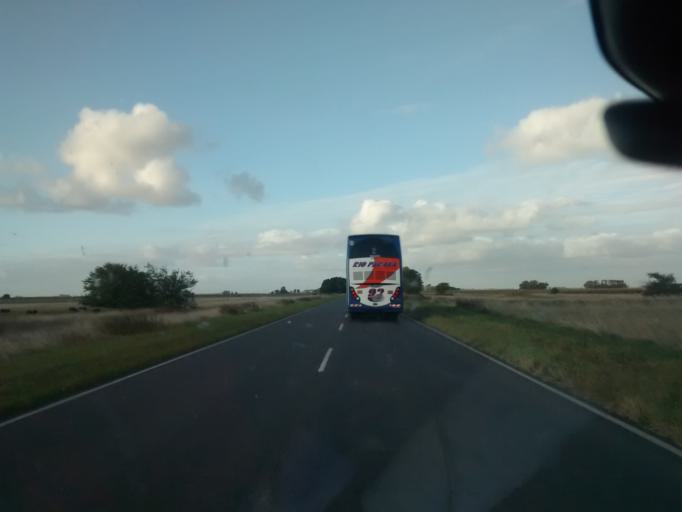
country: AR
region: Buenos Aires
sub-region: Partido de General Belgrano
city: General Belgrano
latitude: -35.8564
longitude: -58.6078
